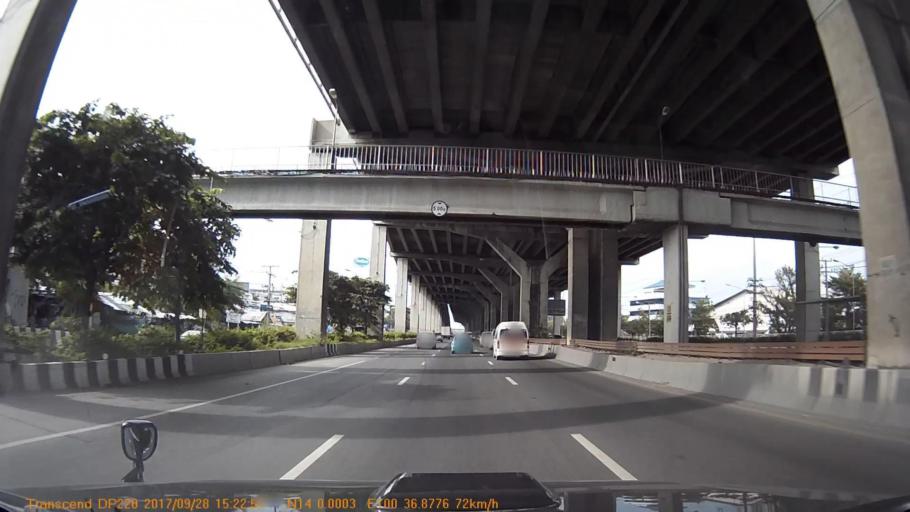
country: TH
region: Phra Nakhon Si Ayutthaya
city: Ban Bang Kadi Pathum Thani
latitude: 14.0004
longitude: 100.6147
